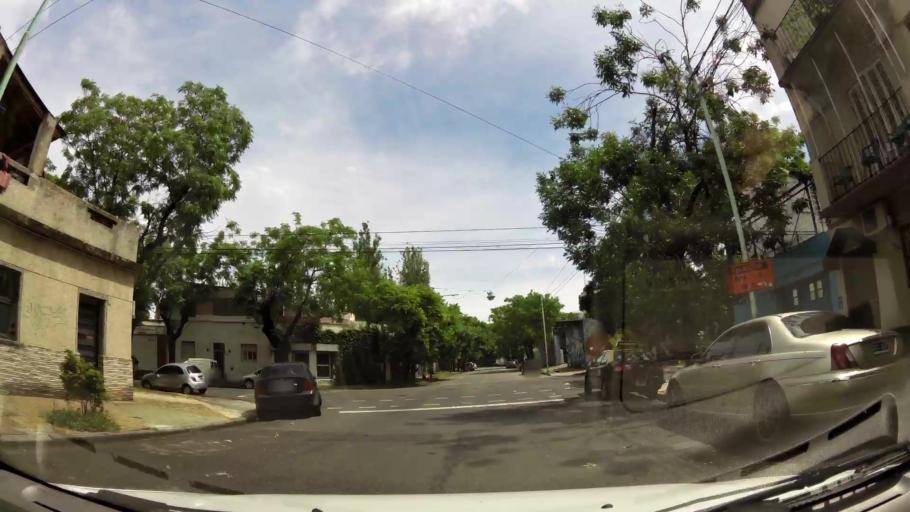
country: AR
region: Buenos Aires F.D.
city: Colegiales
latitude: -34.5882
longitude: -58.4411
